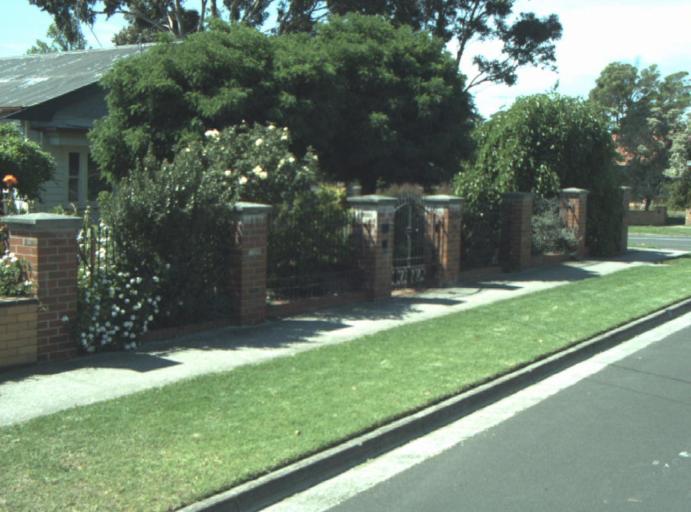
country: AU
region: Victoria
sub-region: Greater Geelong
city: Hamlyn Heights
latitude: -38.1333
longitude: 144.3313
